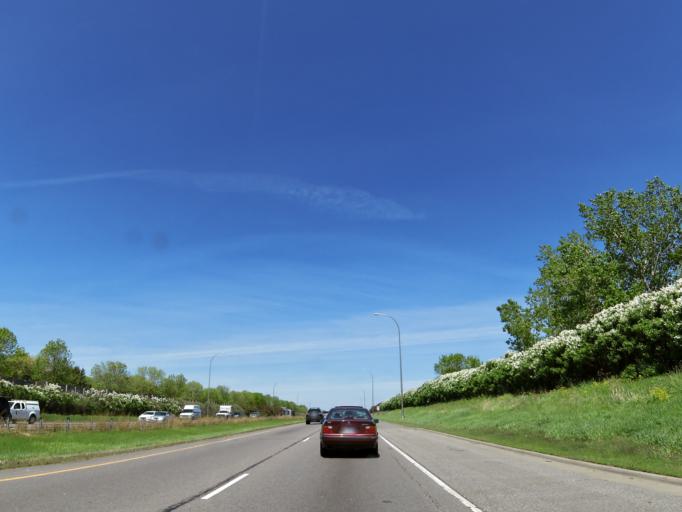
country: US
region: Minnesota
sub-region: Scott County
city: Savage
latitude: 44.8263
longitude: -93.3981
